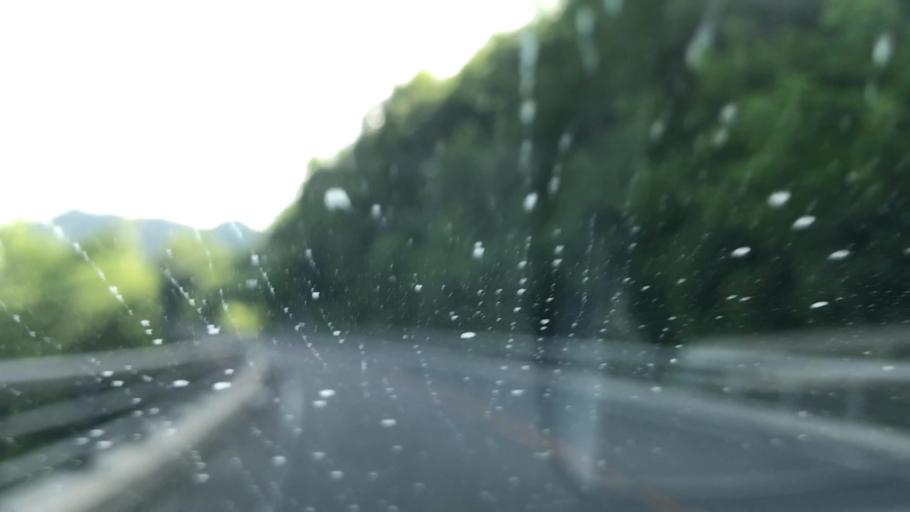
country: JP
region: Hokkaido
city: Shimo-furano
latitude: 42.8415
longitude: 142.4164
